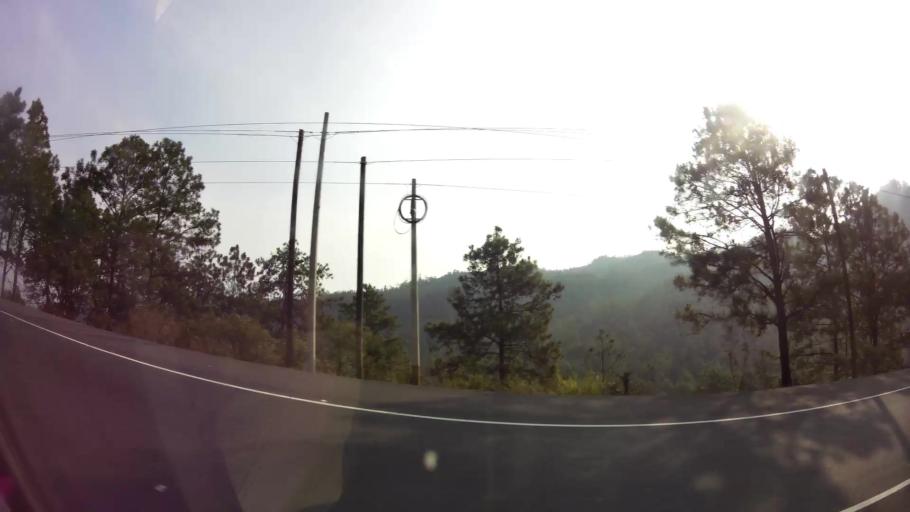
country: HN
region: Comayagua
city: Flores
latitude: 14.2935
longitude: -87.4835
